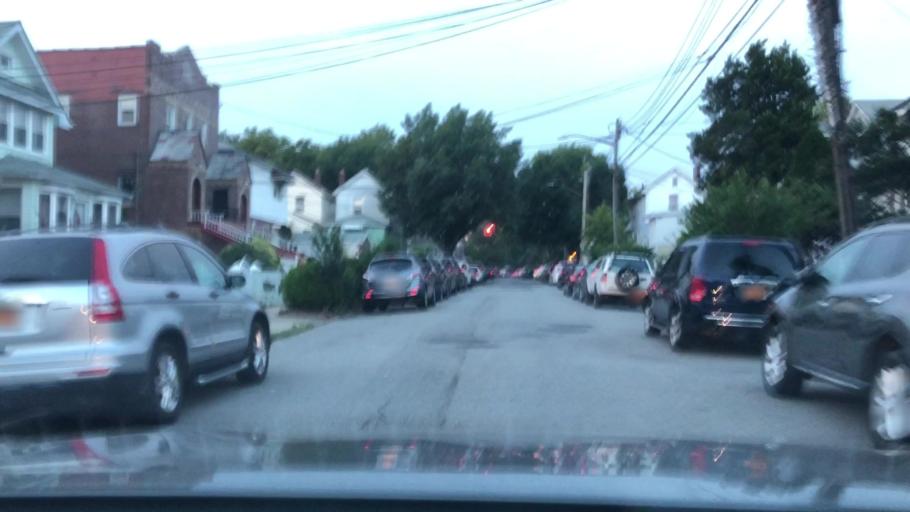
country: US
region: New York
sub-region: Queens County
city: Jamaica
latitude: 40.6787
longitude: -73.8175
